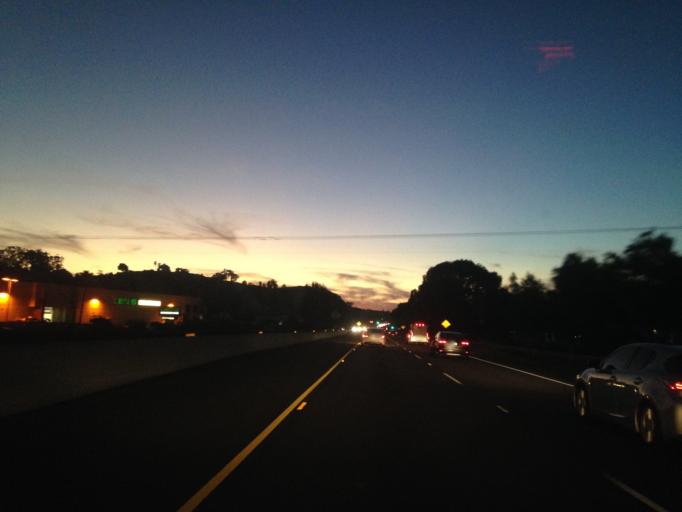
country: US
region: California
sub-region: San Diego County
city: Camp Pendleton South
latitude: 33.2162
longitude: -117.3523
